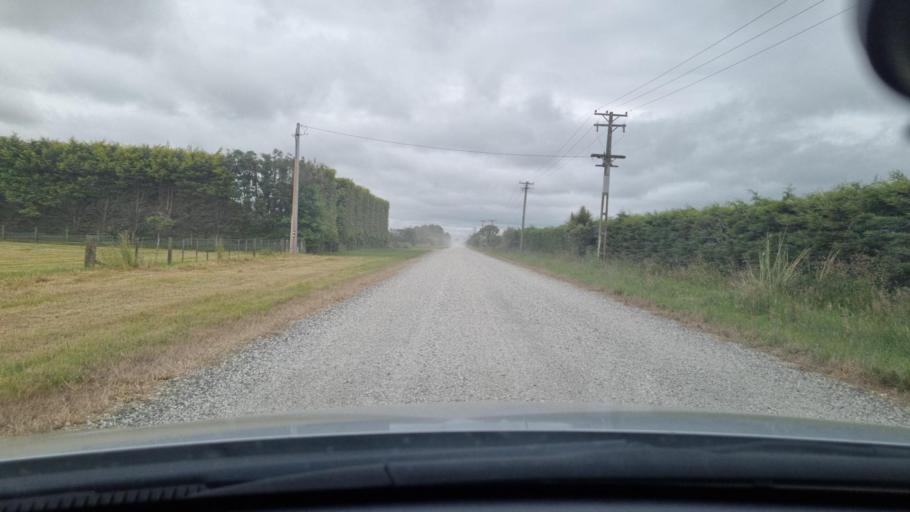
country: NZ
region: Southland
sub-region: Invercargill City
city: Invercargill
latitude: -46.3762
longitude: 168.2985
